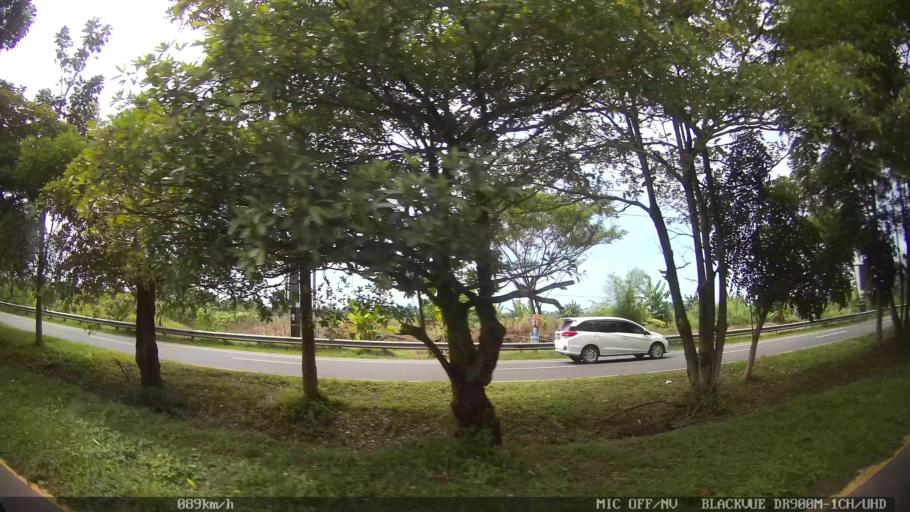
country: ID
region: North Sumatra
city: Percut
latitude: 3.5991
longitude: 98.8266
